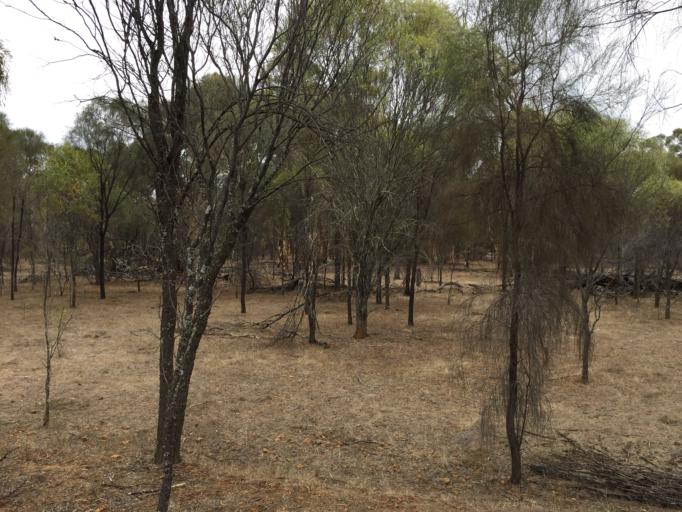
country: AU
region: Western Australia
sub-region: Narrogin
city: Narrogin
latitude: -32.8225
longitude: 116.8894
